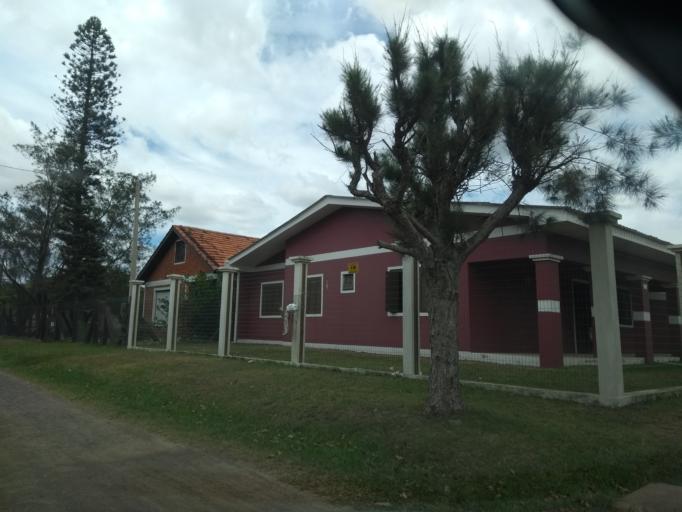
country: BR
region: Rio Grande do Sul
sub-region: Tramandai
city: Tramandai
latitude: -30.0653
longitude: -50.1616
